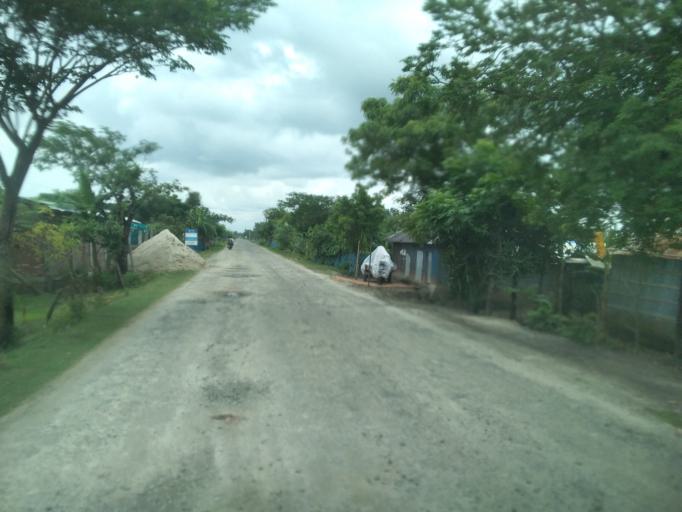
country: IN
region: West Bengal
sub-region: North 24 Parganas
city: Gosaba
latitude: 22.2668
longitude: 89.1773
